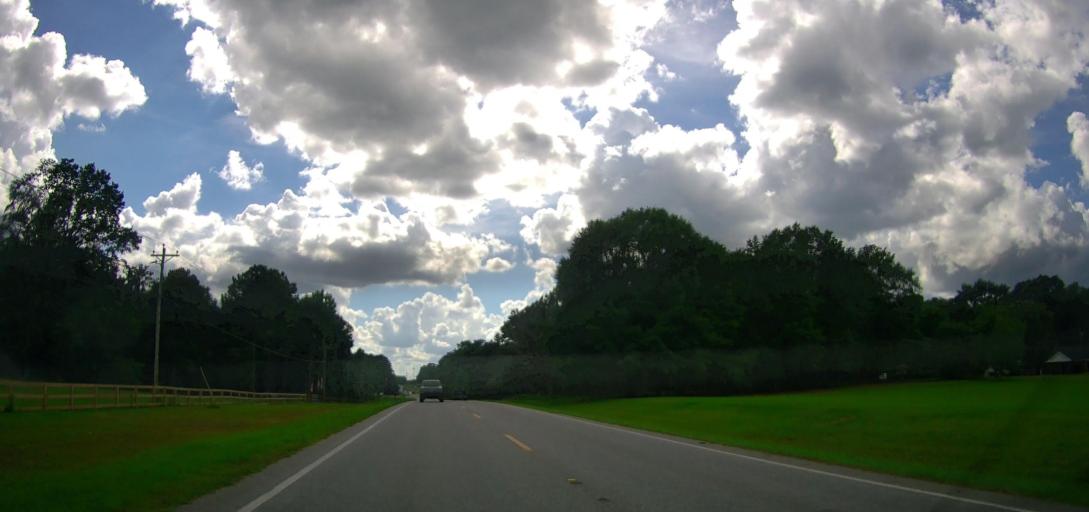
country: US
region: Alabama
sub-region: Russell County
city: Ladonia
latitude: 32.4461
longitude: -85.2522
